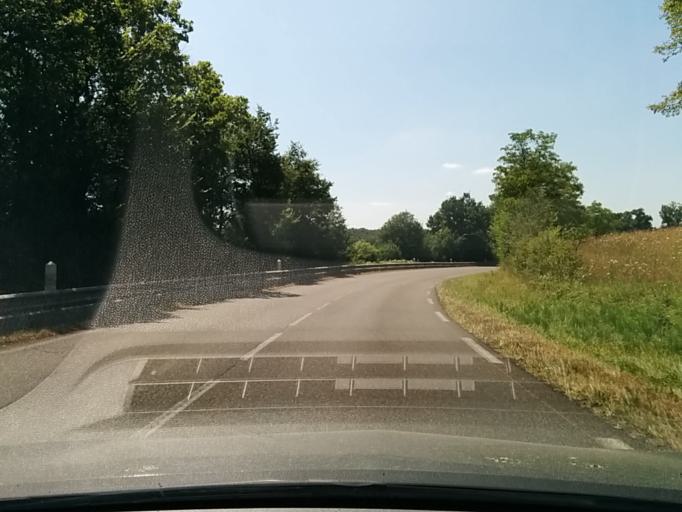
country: FR
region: Midi-Pyrenees
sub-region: Departement du Gers
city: Nogaro
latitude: 43.7487
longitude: -0.0739
